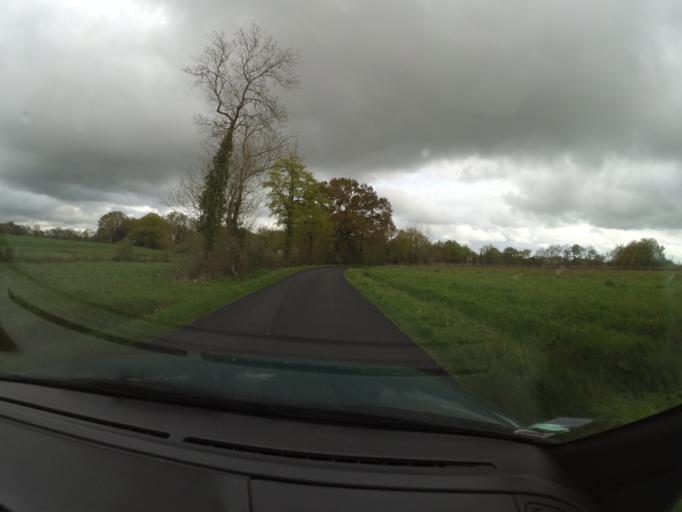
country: FR
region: Pays de la Loire
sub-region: Departement de la Loire-Atlantique
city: Maisdon-sur-Sevre
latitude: 47.0807
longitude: -1.3696
